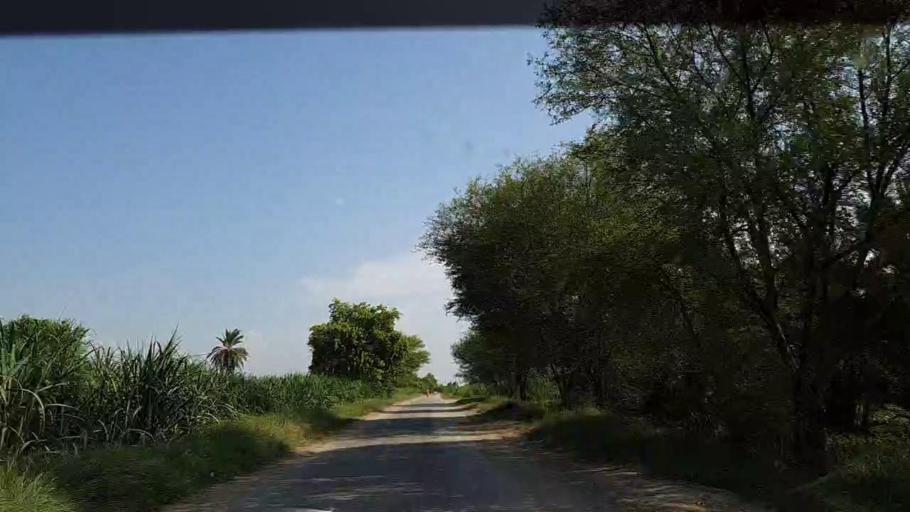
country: PK
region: Sindh
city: Adilpur
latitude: 27.9376
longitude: 69.2540
